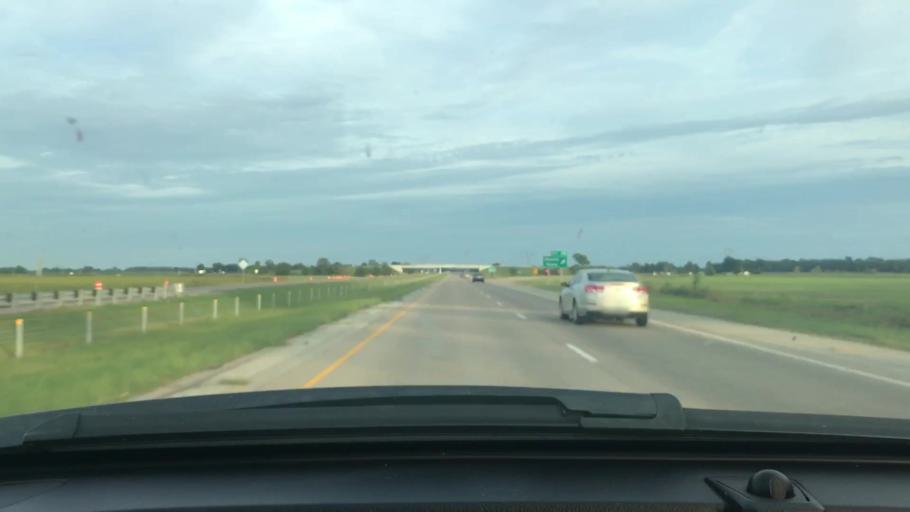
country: US
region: Arkansas
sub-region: Craighead County
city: Bay
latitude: 35.7790
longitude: -90.5921
